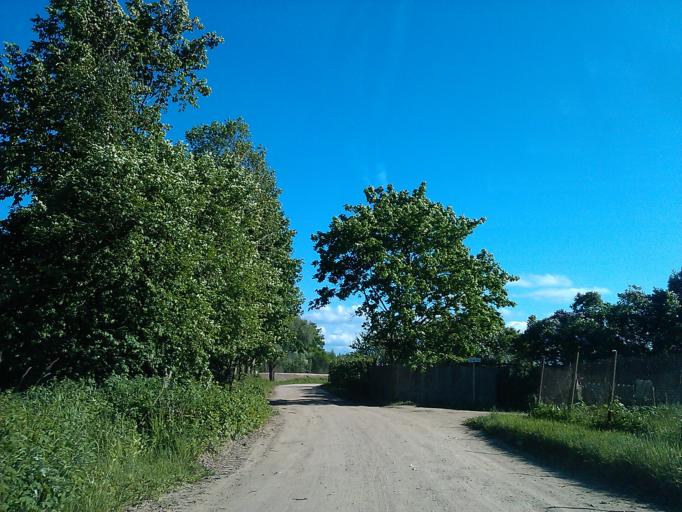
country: LV
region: Adazi
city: Adazi
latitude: 57.0924
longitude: 24.3219
